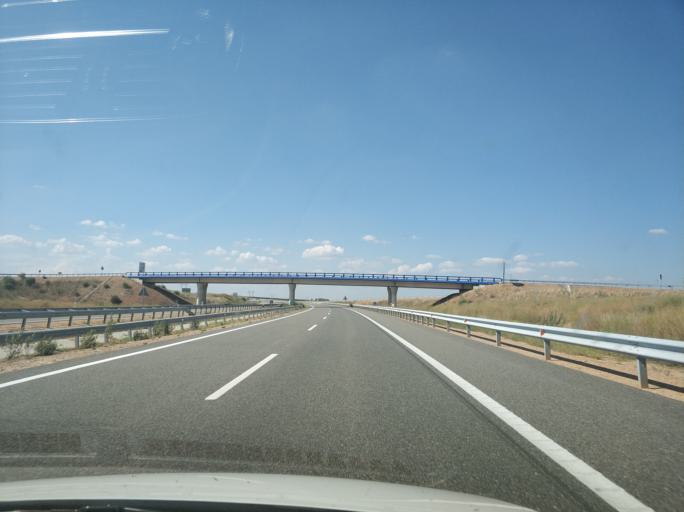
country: ES
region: Castille and Leon
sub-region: Provincia de Zamora
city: Manganeses de la Lampreana
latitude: 41.7615
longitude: -5.7554
